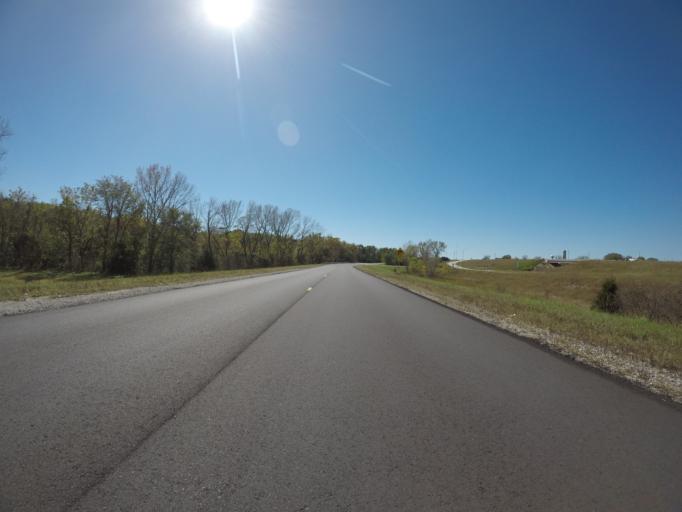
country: US
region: Kansas
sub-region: Douglas County
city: Eudora
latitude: 38.9413
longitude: -95.0704
